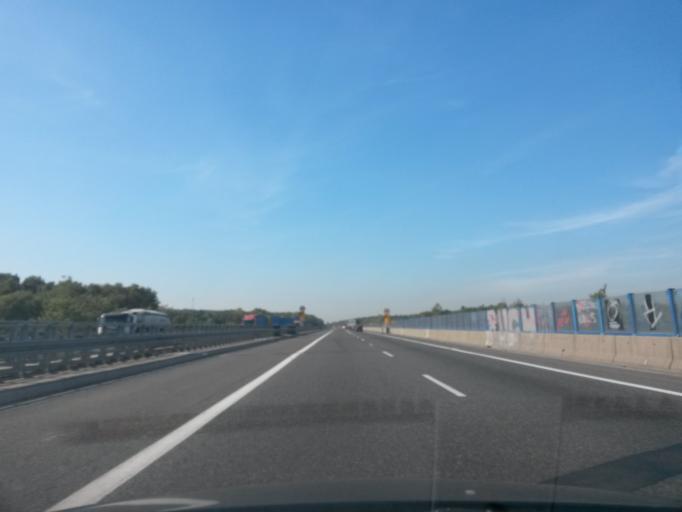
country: PL
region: Silesian Voivodeship
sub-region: Myslowice
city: Myslowice
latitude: 50.2119
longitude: 19.1489
